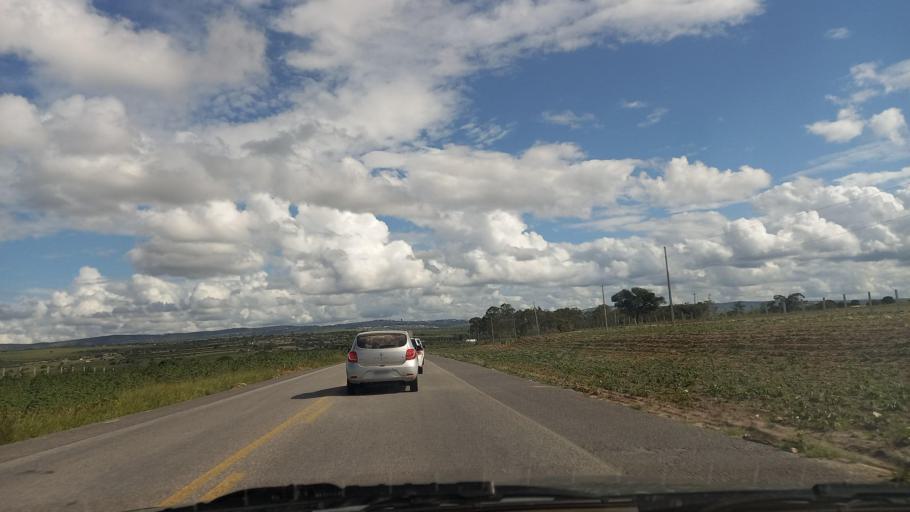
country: BR
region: Pernambuco
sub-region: Sao Joao
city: Sao Joao
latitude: -8.7868
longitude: -36.4331
